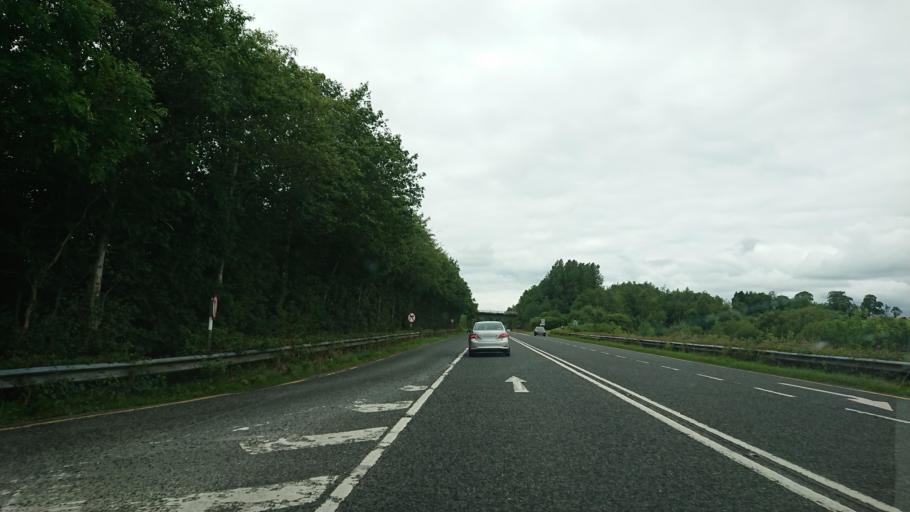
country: IE
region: Connaught
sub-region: County Leitrim
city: Carrick-on-Shannon
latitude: 53.9289
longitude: -8.0004
